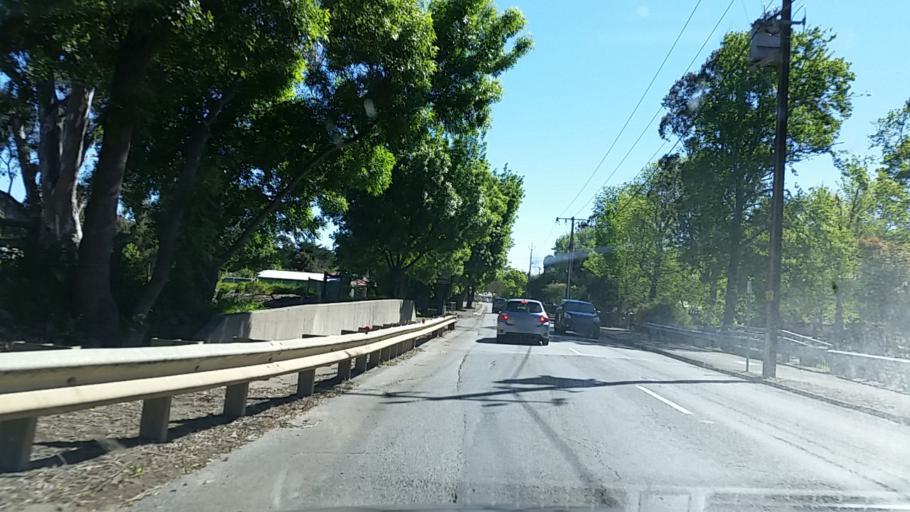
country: AU
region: South Australia
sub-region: Mount Barker
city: Meadows
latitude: -35.1818
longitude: 138.7581
